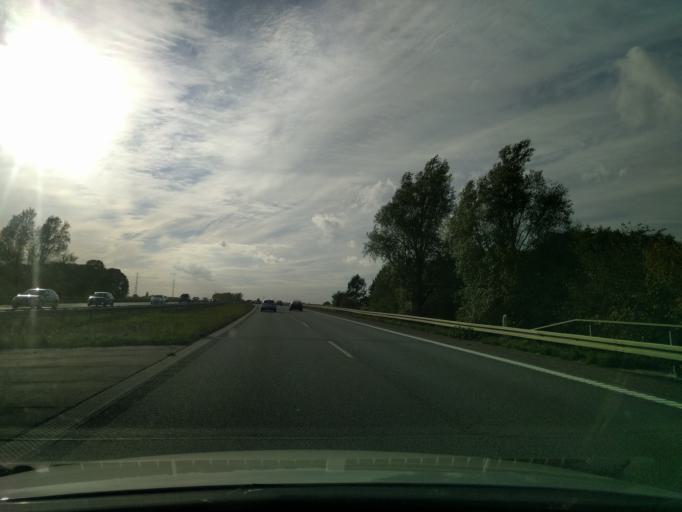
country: DK
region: Zealand
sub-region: Koge Kommune
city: Borup
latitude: 55.4563
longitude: 11.8920
